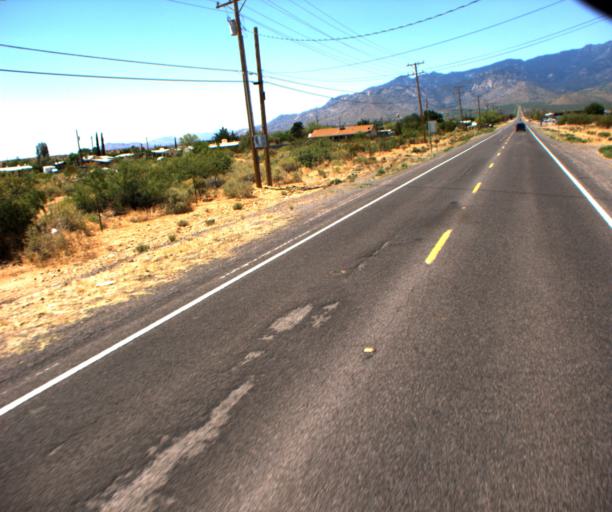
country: US
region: Arizona
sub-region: Graham County
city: Swift Trail Junction
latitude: 32.7276
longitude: -109.7166
